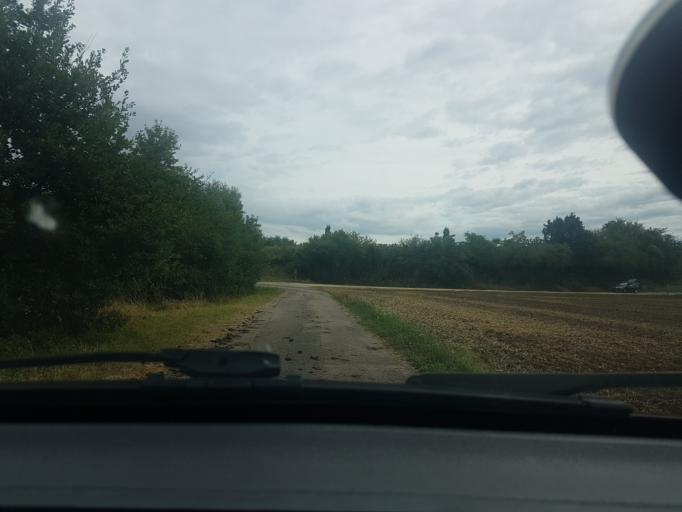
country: FR
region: Bourgogne
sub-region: Departement de Saone-et-Loire
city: Rully
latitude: 46.8817
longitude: 4.7621
